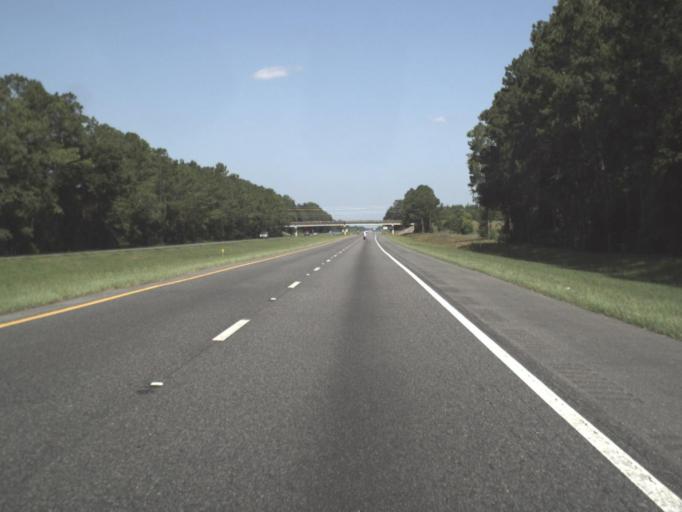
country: US
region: Florida
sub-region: Suwannee County
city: Live Oak
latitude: 30.3419
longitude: -83.1260
